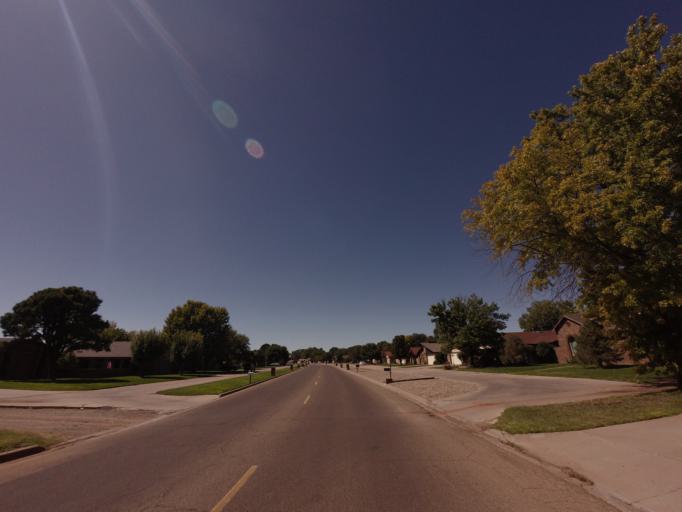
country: US
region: New Mexico
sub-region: Curry County
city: Clovis
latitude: 34.4410
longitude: -103.1828
